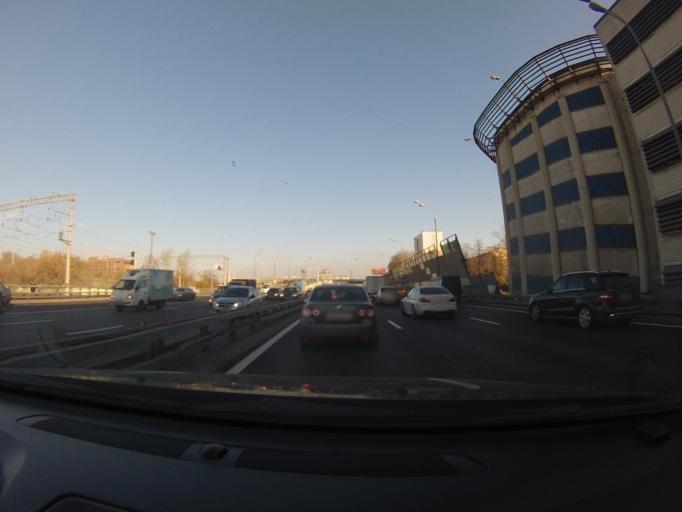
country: RU
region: Moskovskaya
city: Presnenskiy
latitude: 55.7631
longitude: 37.5361
